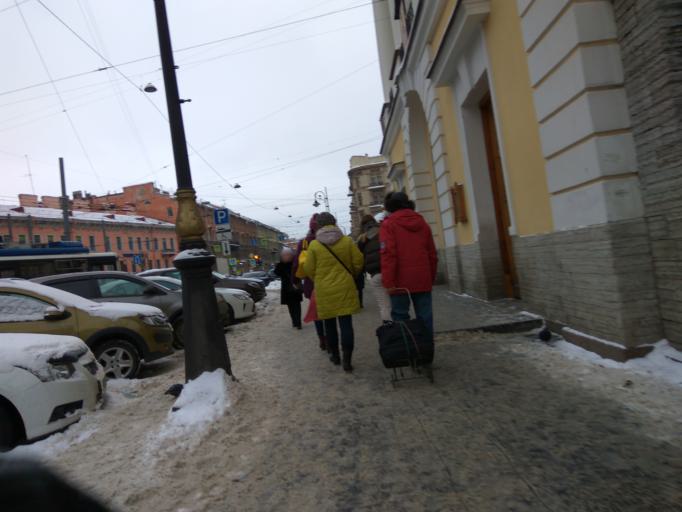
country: RU
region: St.-Petersburg
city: Centralniy
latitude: 59.9280
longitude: 30.3478
